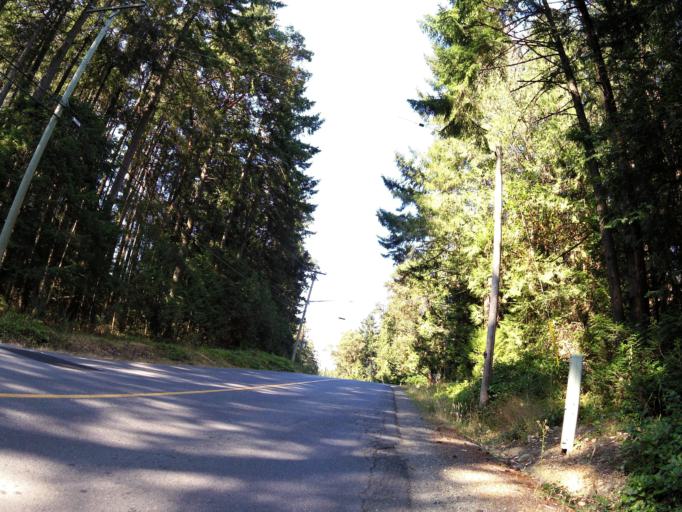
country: CA
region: British Columbia
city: North Saanich
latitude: 48.6680
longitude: -123.5532
